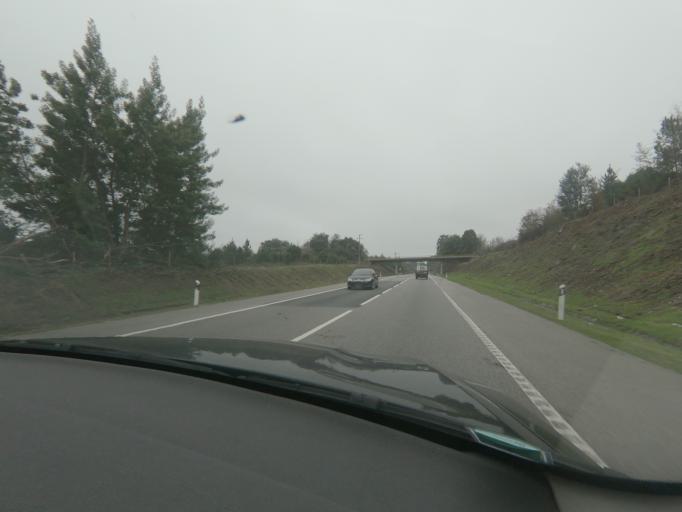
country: PT
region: Viseu
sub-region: Concelho de Tondela
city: Tondela
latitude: 40.5752
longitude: -8.0317
